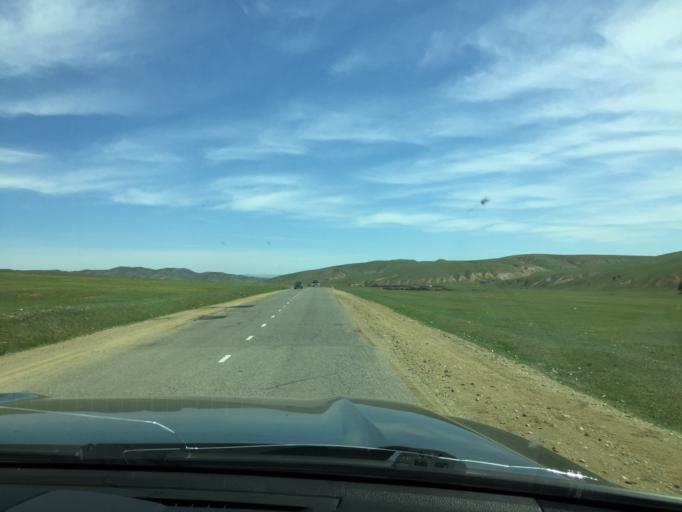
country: MN
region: Central Aimak
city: Bornuur
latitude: 48.6608
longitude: 106.1220
